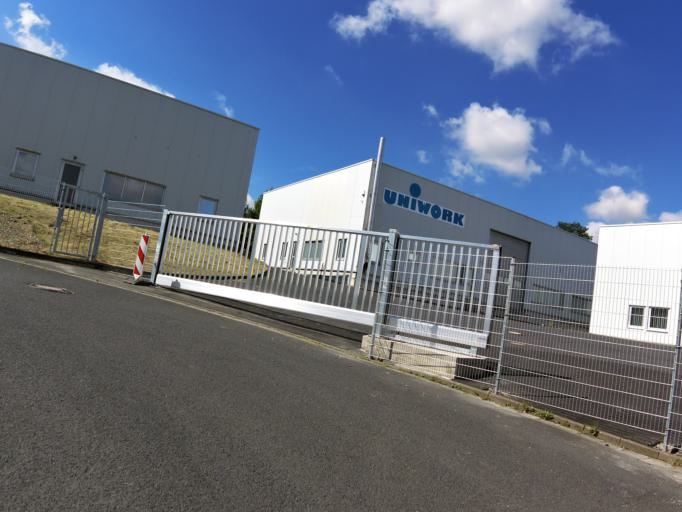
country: DE
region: Thuringia
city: Krauthausen
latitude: 51.0132
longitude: 10.2459
